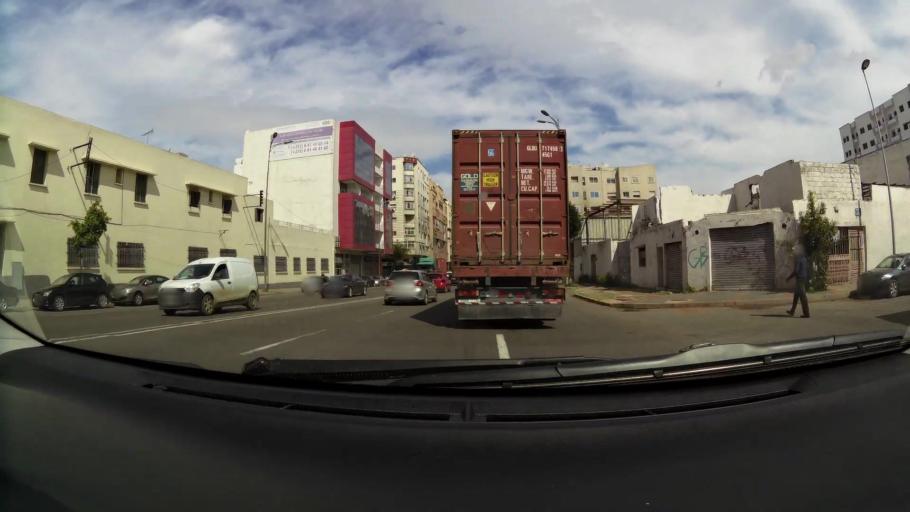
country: MA
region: Grand Casablanca
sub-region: Casablanca
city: Casablanca
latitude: 33.5866
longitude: -7.6003
